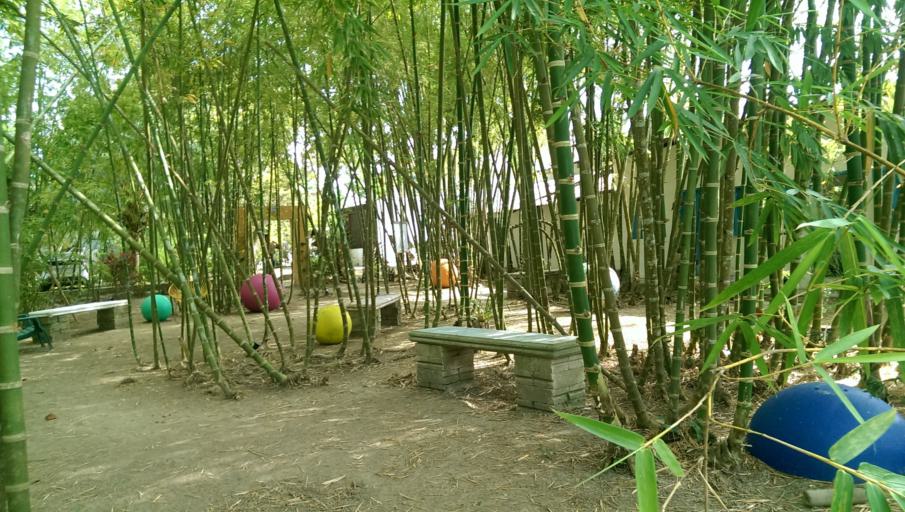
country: MX
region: Veracruz
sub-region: Tuxpan
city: Tierra Blanca
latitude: 20.9145
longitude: -97.4643
